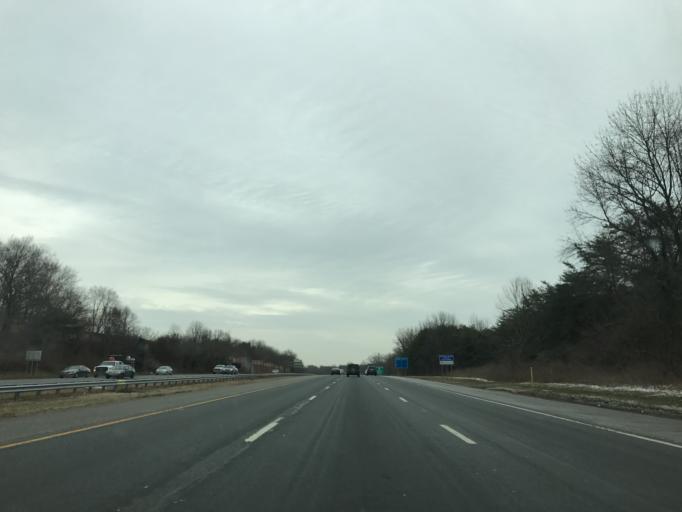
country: US
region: New Jersey
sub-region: Camden County
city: Ellisburg
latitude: 39.8913
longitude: -74.9987
